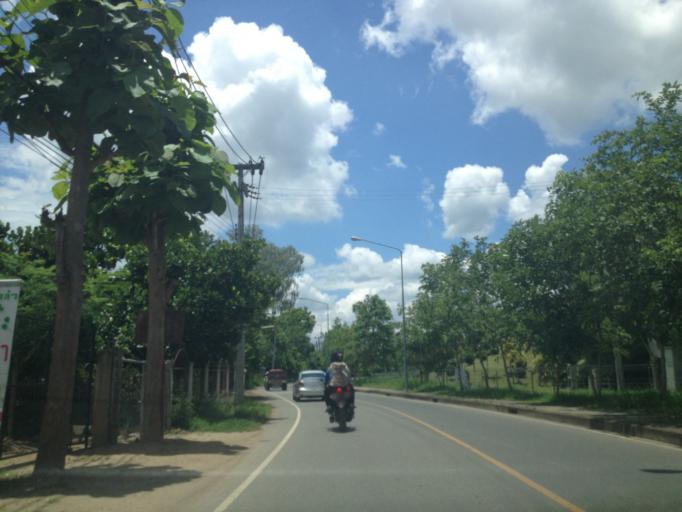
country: TH
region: Chiang Mai
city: Hang Dong
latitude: 18.7487
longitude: 98.9271
